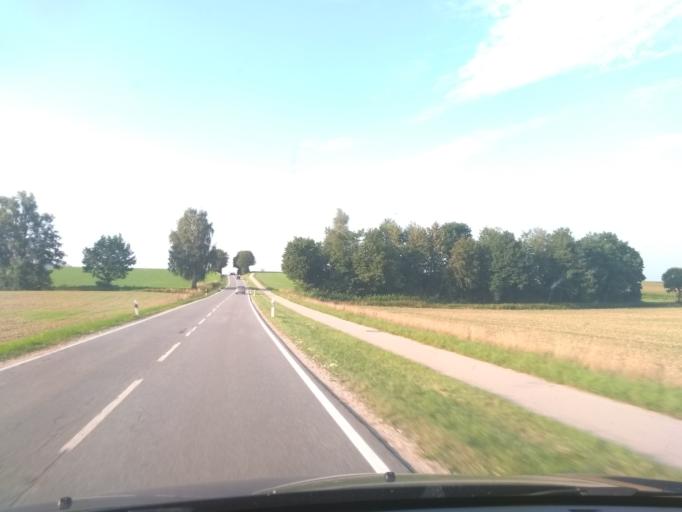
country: DE
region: Bavaria
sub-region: Upper Bavaria
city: Markt Indersdorf
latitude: 48.3316
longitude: 11.3880
